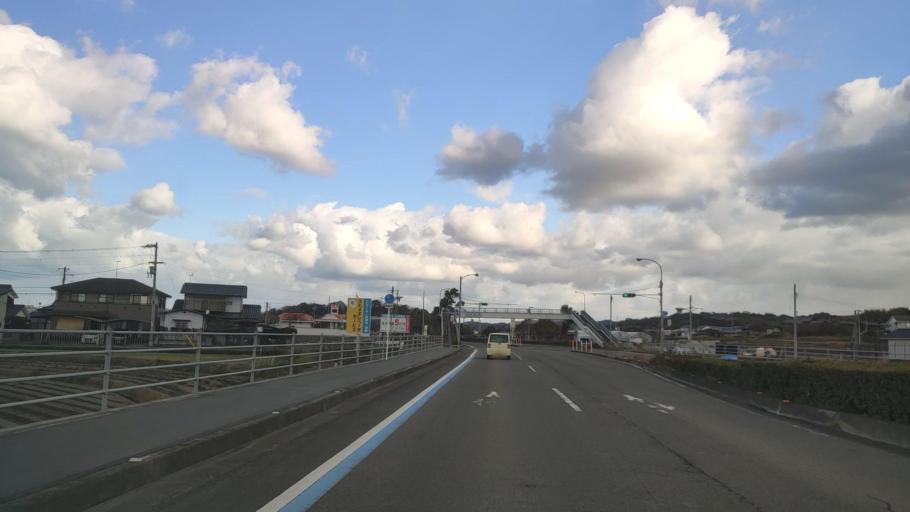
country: JP
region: Ehime
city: Hojo
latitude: 33.9422
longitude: 132.7748
